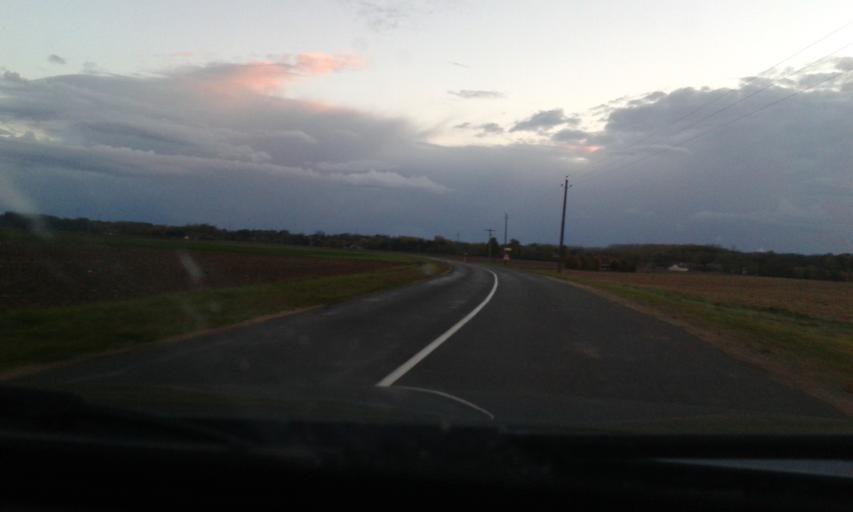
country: FR
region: Centre
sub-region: Departement du Loiret
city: Huisseau-sur-Mauves
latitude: 47.8745
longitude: 1.6960
